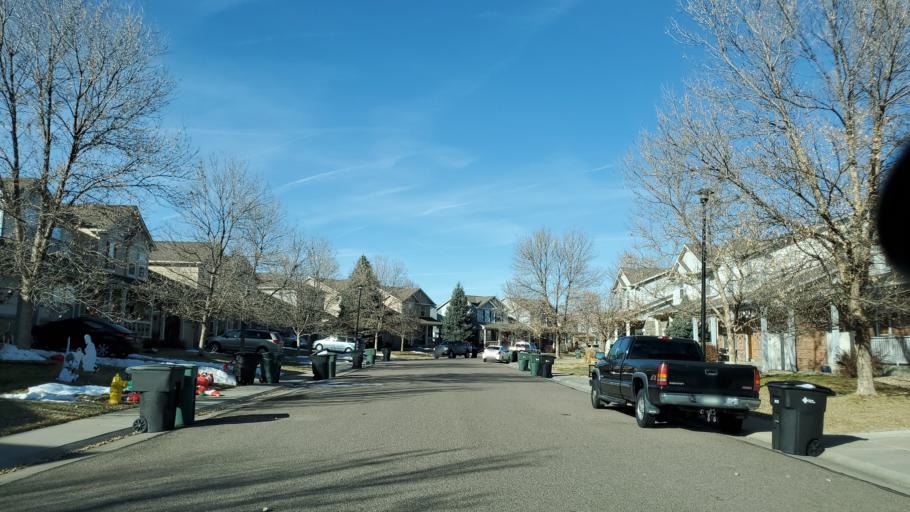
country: US
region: Colorado
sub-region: Adams County
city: Northglenn
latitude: 39.9198
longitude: -104.9466
